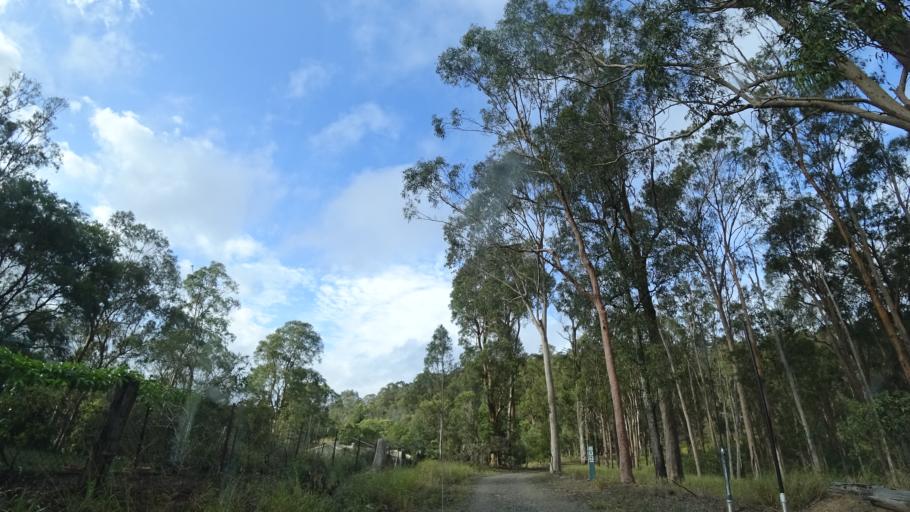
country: AU
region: Queensland
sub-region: Moreton Bay
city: Ferny Hills
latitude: -27.4497
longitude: 152.9278
